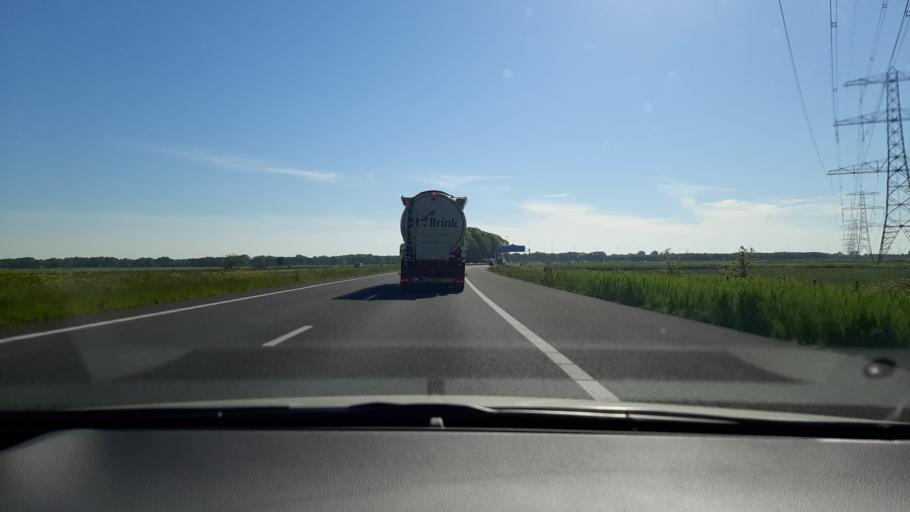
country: NL
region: Drenthe
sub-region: Gemeente Coevorden
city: Dalen
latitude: 52.7290
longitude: 6.7699
